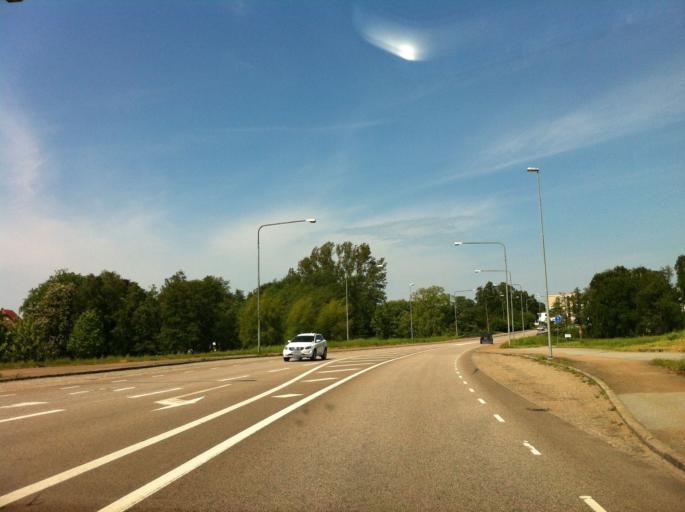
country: SE
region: Skane
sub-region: Helsingborg
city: Glumslov
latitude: 55.9365
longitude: 12.8477
